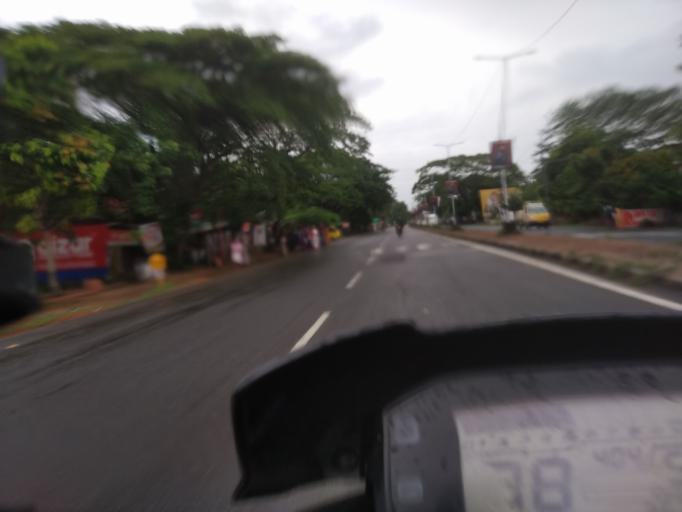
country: IN
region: Kerala
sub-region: Alappuzha
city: Kutiatodu
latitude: 9.7543
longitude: 76.3184
